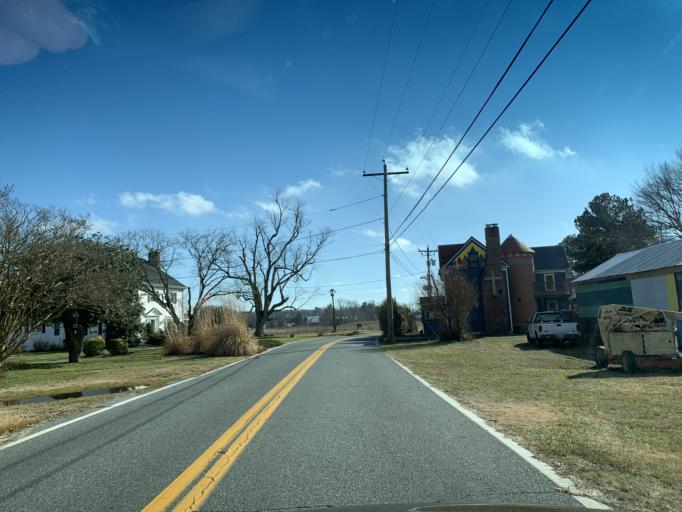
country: US
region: Delaware
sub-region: Sussex County
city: Selbyville
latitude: 38.4507
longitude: -75.1948
